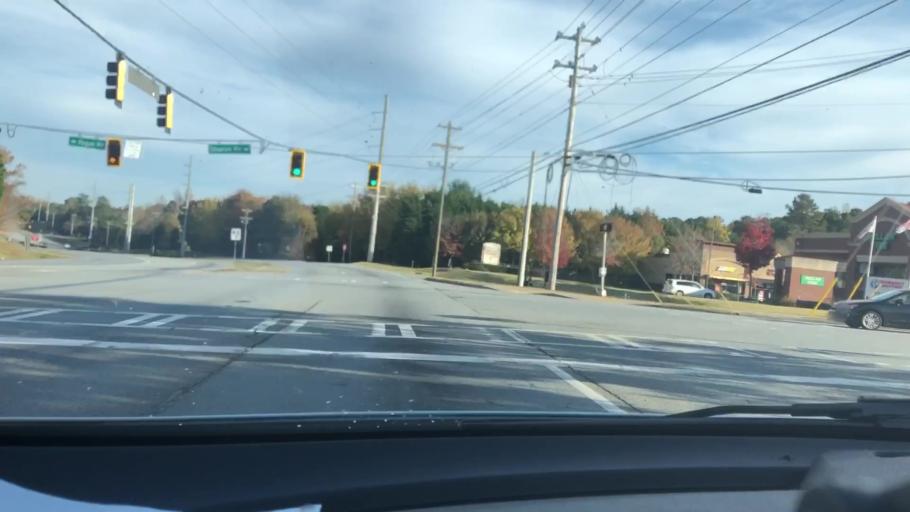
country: US
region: Georgia
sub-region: Forsyth County
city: Cumming
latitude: 34.1243
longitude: -84.1709
